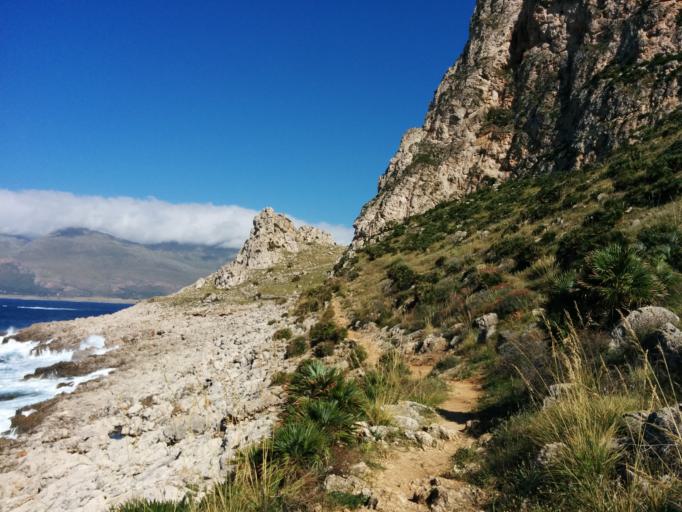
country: IT
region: Sicily
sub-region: Trapani
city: Custonaci
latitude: 38.1137
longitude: 12.6743
